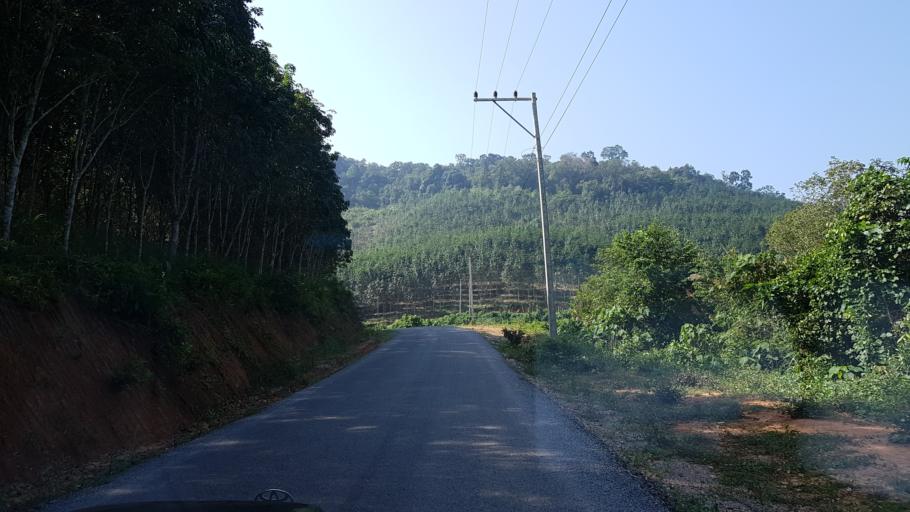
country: LA
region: Oudomxai
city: Muang Xay
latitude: 20.7136
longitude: 102.0733
